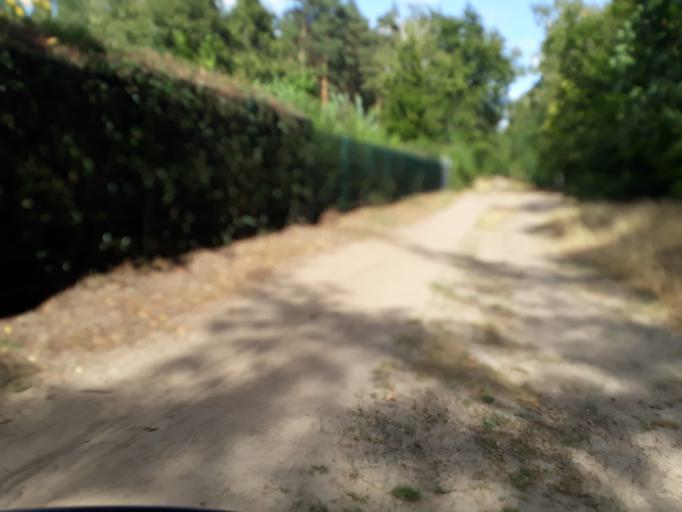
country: DE
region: Berlin
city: Grunewald
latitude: 52.4925
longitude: 13.2512
